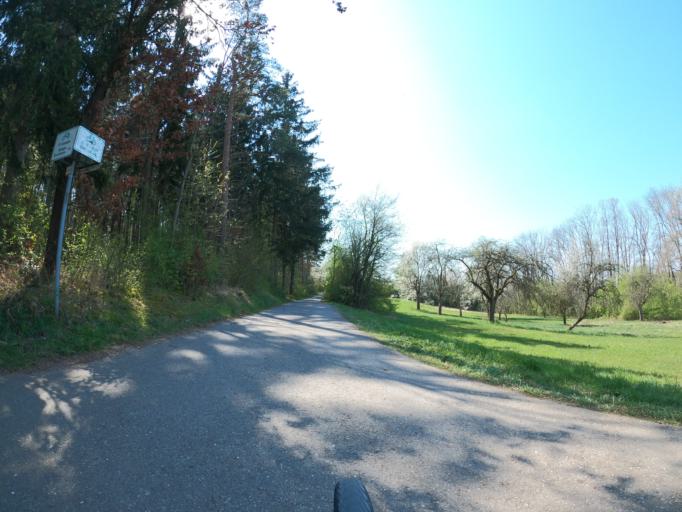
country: DE
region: Baden-Wuerttemberg
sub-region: Tuebingen Region
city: Wannweil
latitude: 48.4822
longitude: 9.1575
